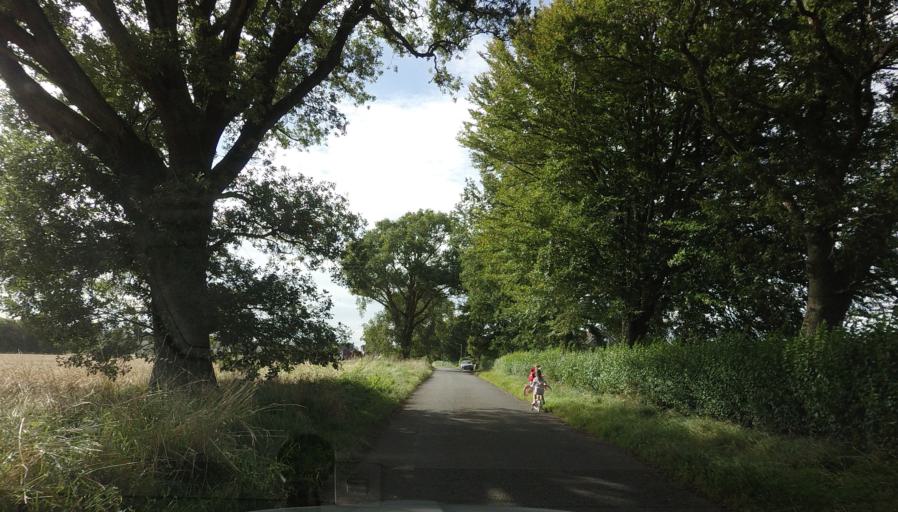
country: GB
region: Scotland
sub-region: Perth and Kinross
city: Bridge of Earn
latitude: 56.3457
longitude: -3.3886
